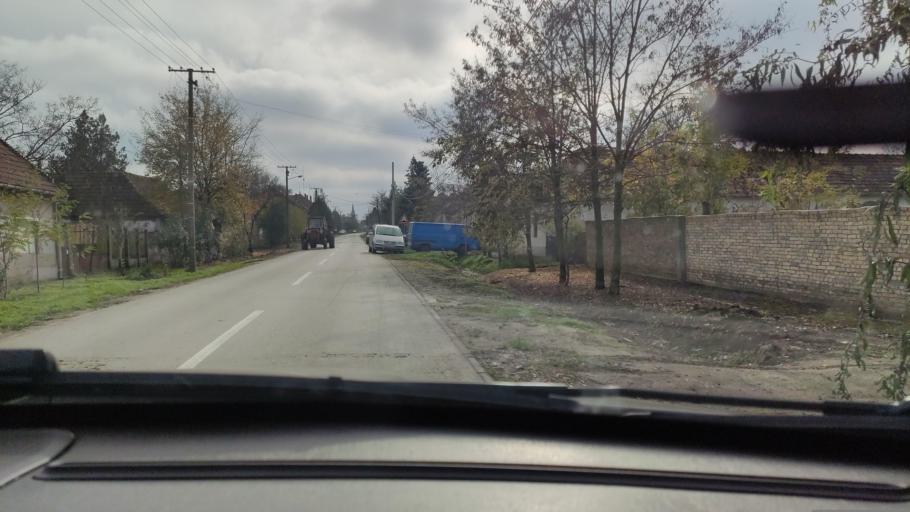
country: RS
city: Jazovo
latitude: 45.9012
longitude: 20.2169
